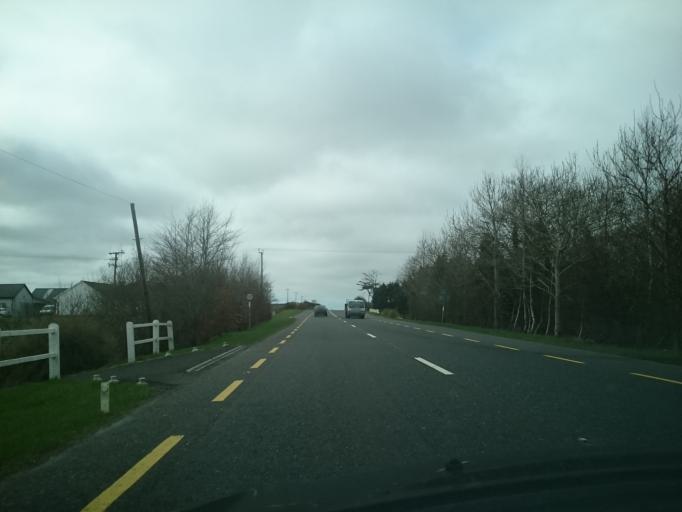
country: IE
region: Connaught
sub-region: Maigh Eo
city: Westport
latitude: 53.8033
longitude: -9.4751
